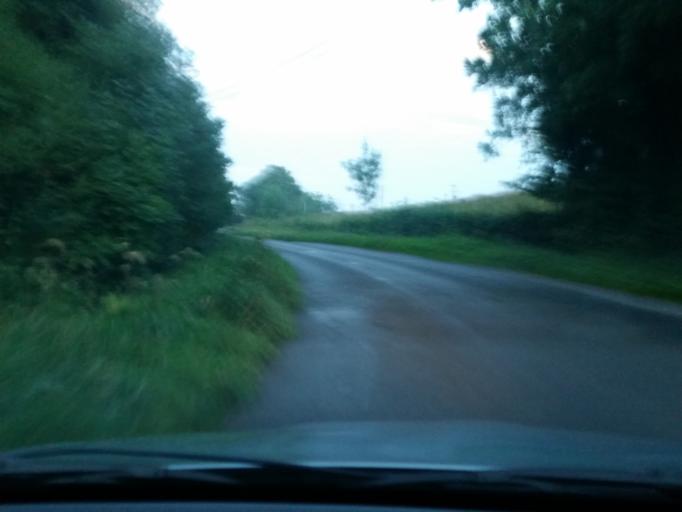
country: IE
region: Ulster
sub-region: County Monaghan
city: Clones
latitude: 54.2372
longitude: -7.2648
